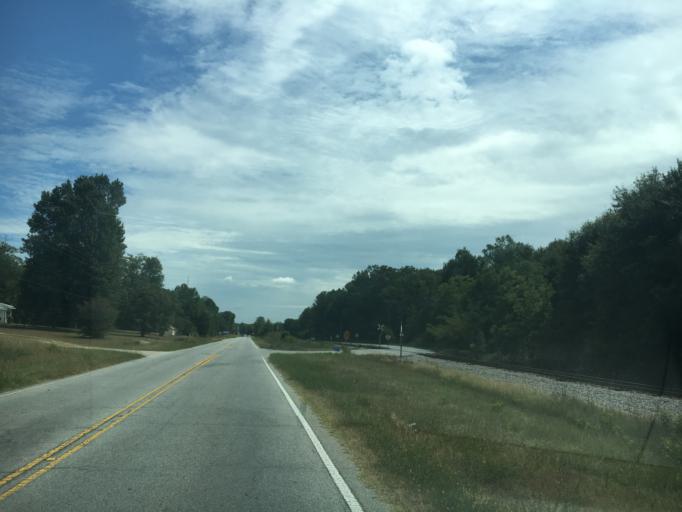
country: US
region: South Carolina
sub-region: Laurens County
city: Laurens
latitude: 34.5390
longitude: -82.0645
